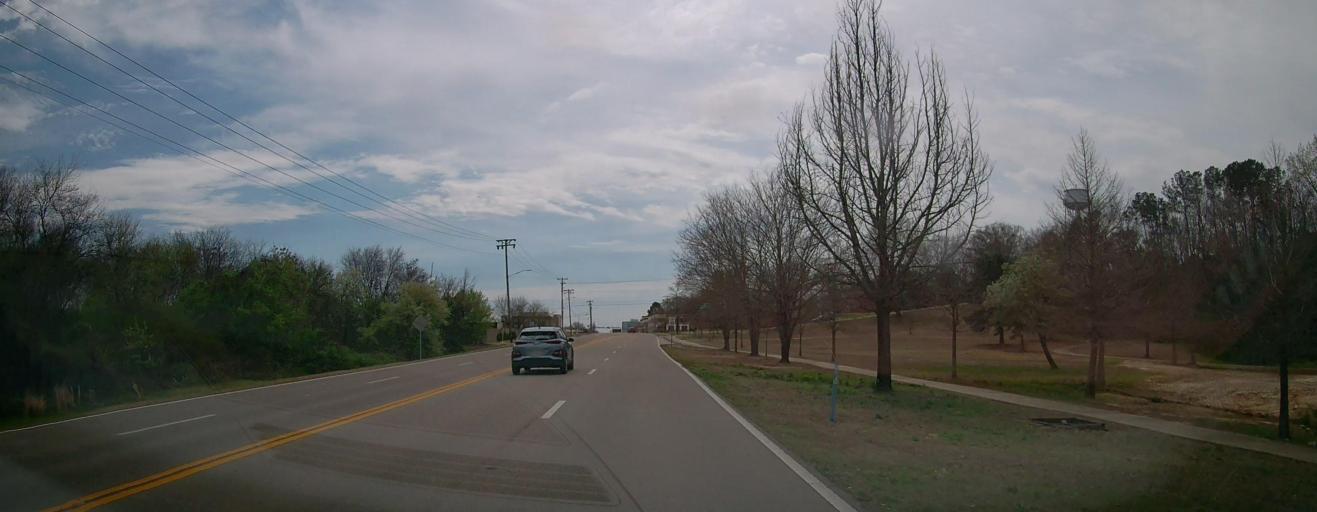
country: US
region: Mississippi
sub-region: Lee County
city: Tupelo
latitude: 34.2661
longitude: -88.7036
